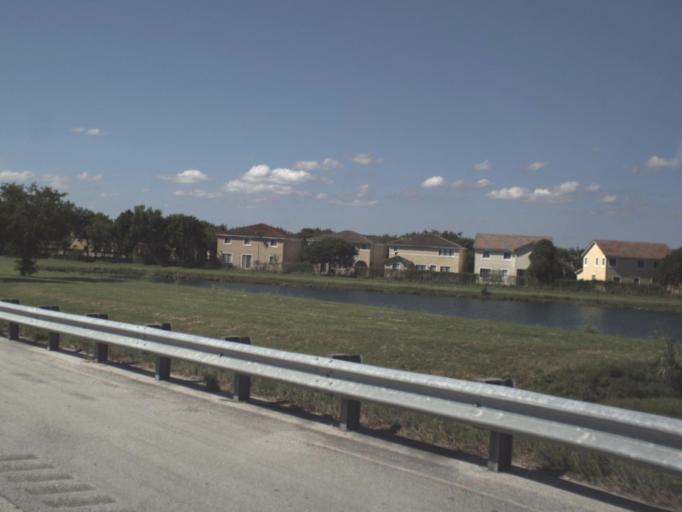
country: US
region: Florida
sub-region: Miami-Dade County
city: Naranja
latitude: 25.5088
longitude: -80.4149
